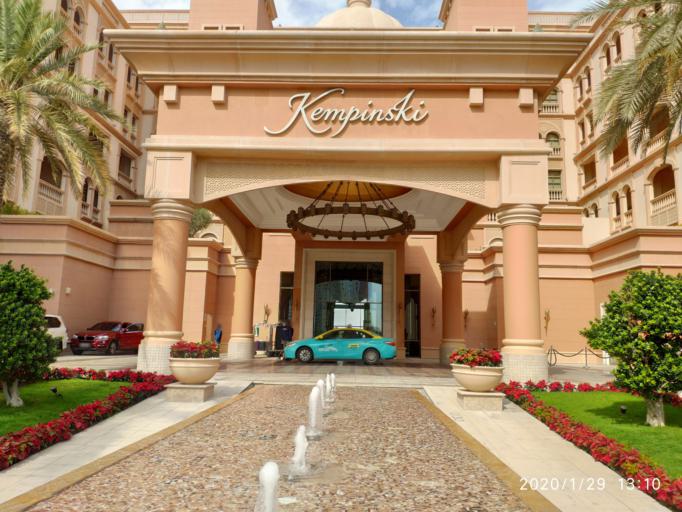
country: QA
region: Baladiyat ad Dawhah
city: Doha
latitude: 25.3754
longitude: 51.5497
